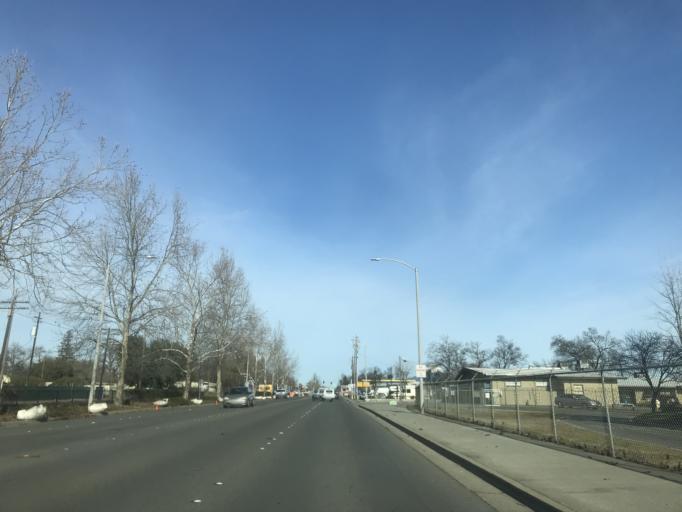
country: US
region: California
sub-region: Yolo County
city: Woodland
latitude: 38.6656
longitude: -121.7656
